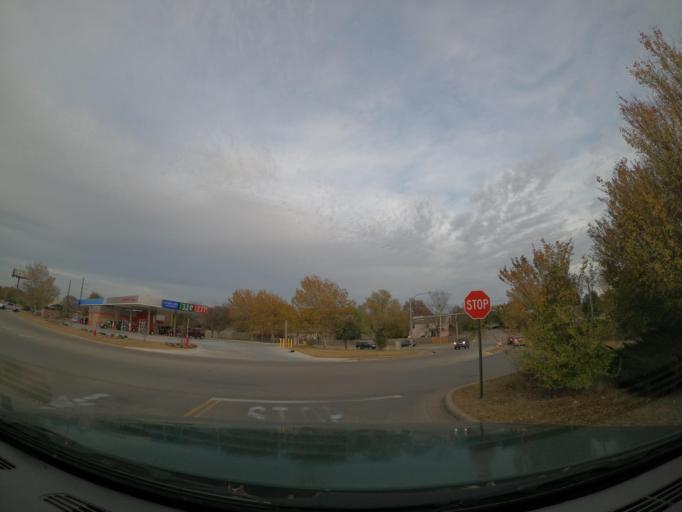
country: US
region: Oklahoma
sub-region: Tulsa County
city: Broken Arrow
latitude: 35.9904
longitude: -95.7981
